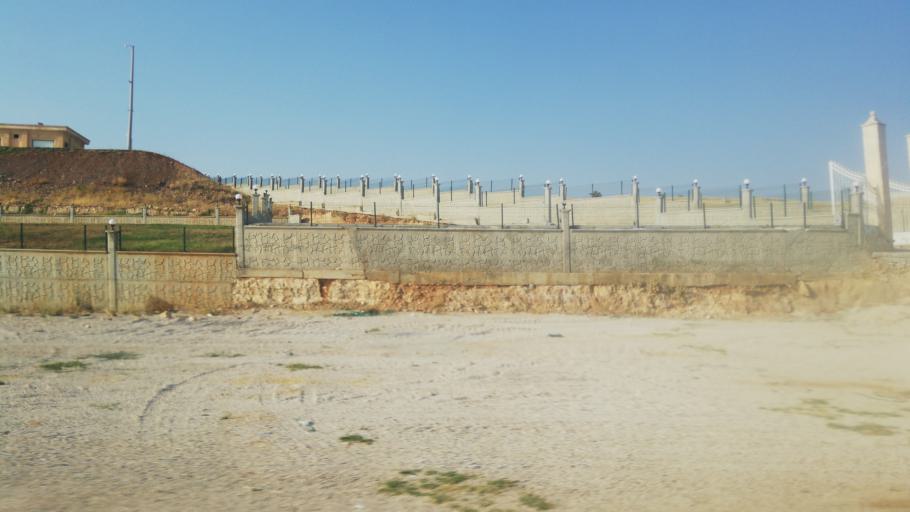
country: TR
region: Mardin
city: Kindirip
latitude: 37.4561
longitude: 41.2455
